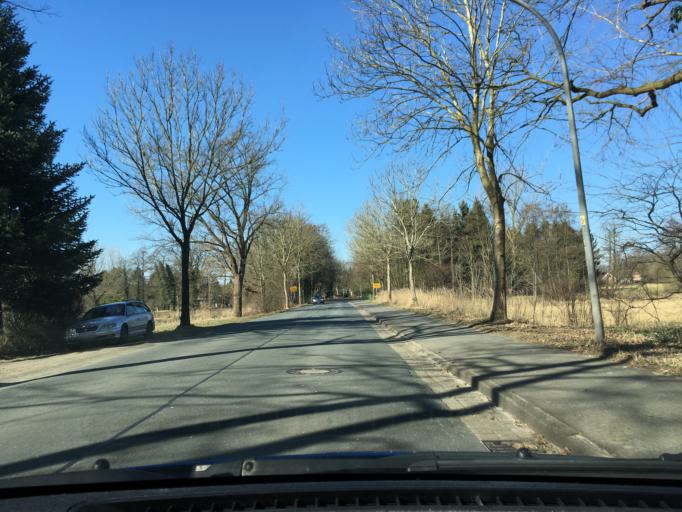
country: DE
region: Lower Saxony
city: Hemslingen
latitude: 53.0814
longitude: 9.6045
